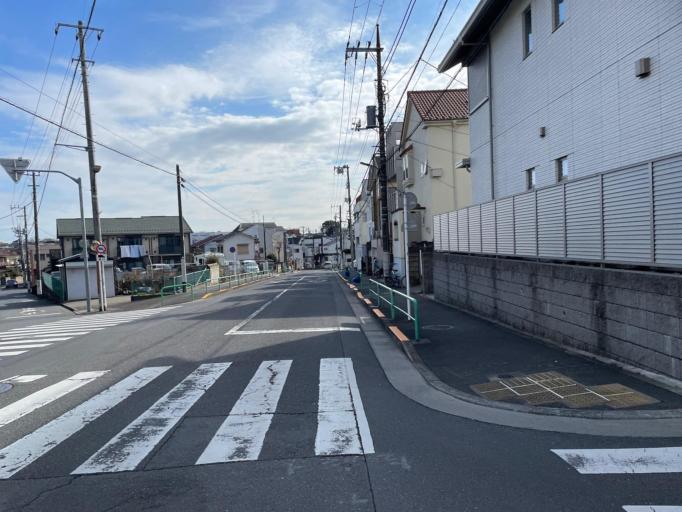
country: JP
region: Saitama
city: Wako
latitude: 35.7605
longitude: 139.6658
